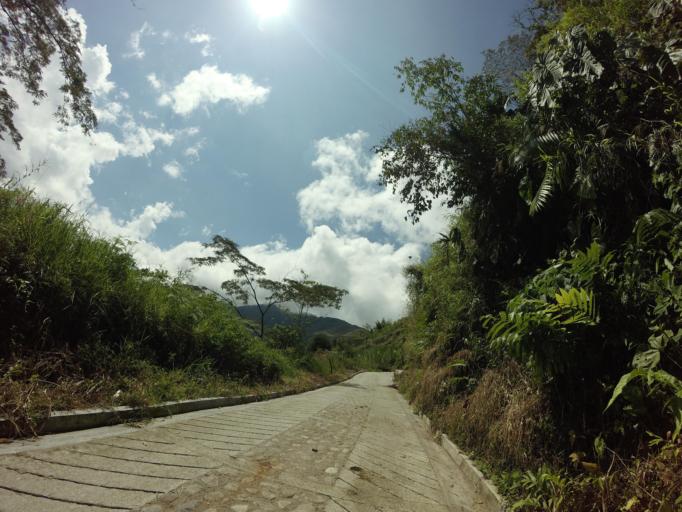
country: CO
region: Caldas
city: Pensilvania
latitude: 5.4830
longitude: -75.1782
